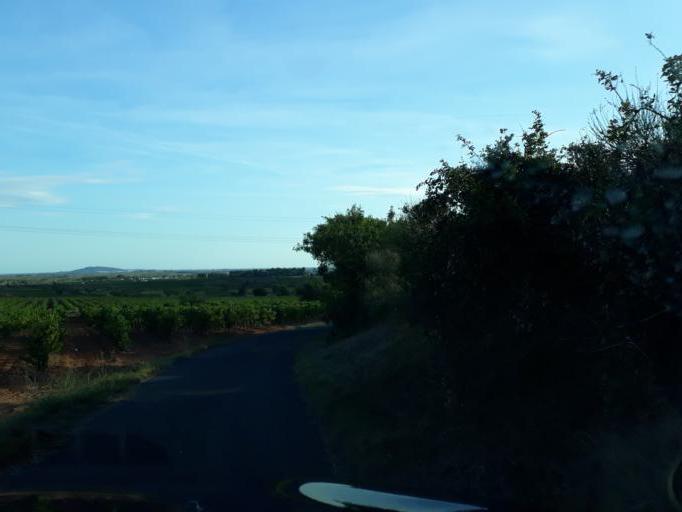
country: FR
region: Languedoc-Roussillon
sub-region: Departement de l'Herault
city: Florensac
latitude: 43.4170
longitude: 3.4742
